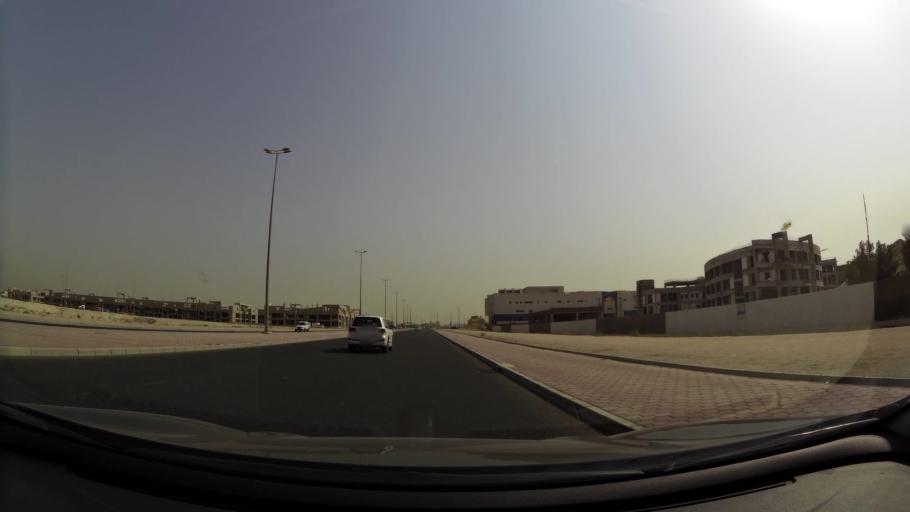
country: KW
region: Al Asimah
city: Ar Rabiyah
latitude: 29.2887
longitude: 47.9085
